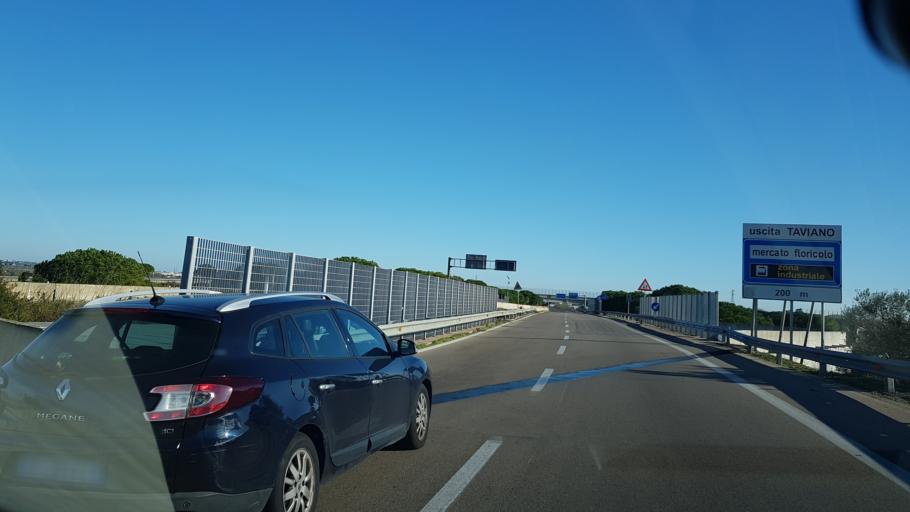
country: IT
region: Apulia
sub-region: Provincia di Lecce
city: Taviano
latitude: 40.0016
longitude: 18.0623
